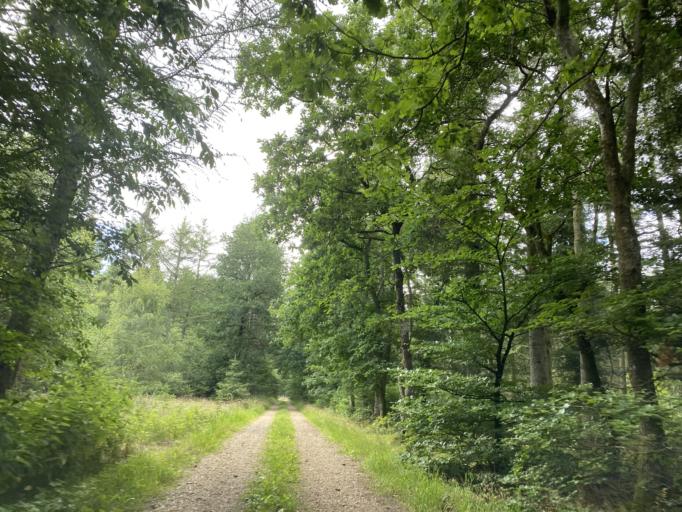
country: DK
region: Central Jutland
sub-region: Viborg Kommune
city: Bjerringbro
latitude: 56.2702
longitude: 9.6522
